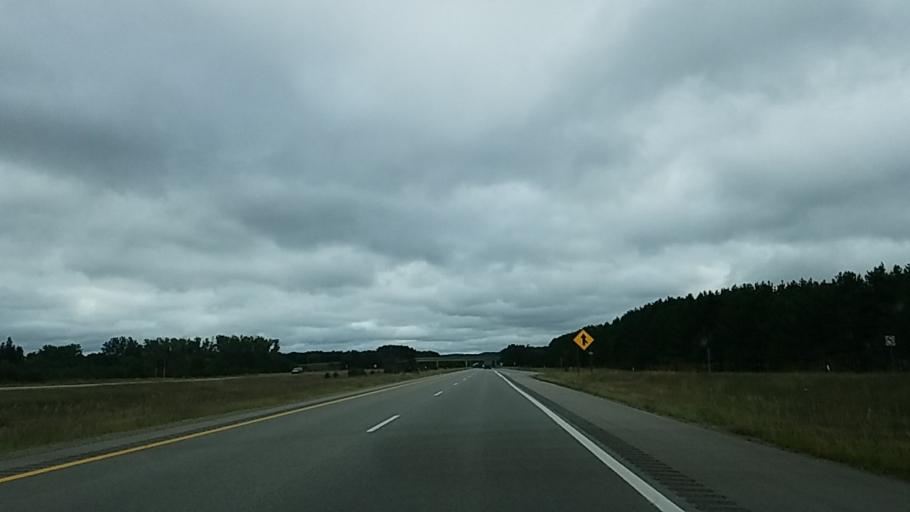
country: US
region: Michigan
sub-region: Otsego County
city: Gaylord
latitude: 45.1473
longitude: -84.6704
